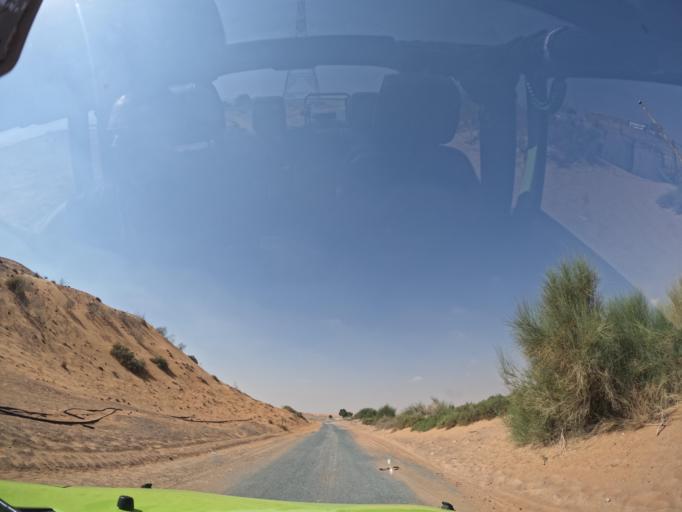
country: AE
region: Ash Shariqah
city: Adh Dhayd
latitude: 24.8005
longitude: 55.7980
